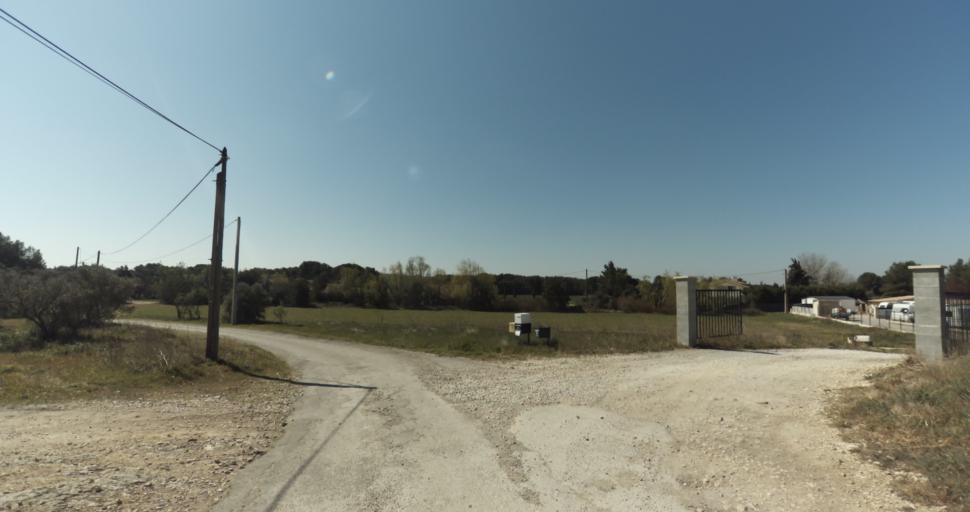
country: FR
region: Provence-Alpes-Cote d'Azur
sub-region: Departement des Bouches-du-Rhone
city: Pelissanne
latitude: 43.6185
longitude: 5.1568
